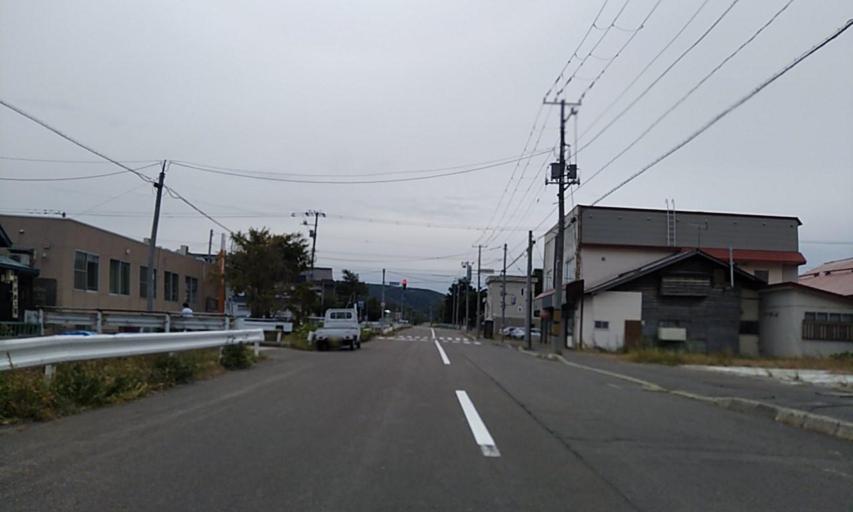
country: JP
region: Hokkaido
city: Rumoi
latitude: 43.8565
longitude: 141.5218
